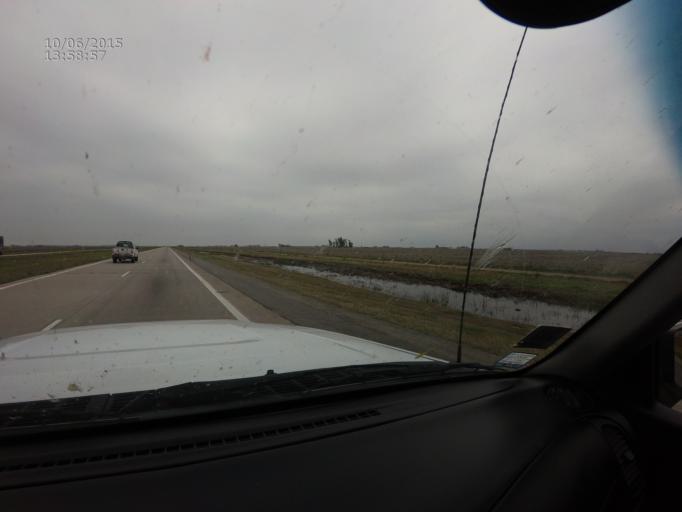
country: AR
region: Cordoba
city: Morrison
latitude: -32.5492
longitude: -62.8610
